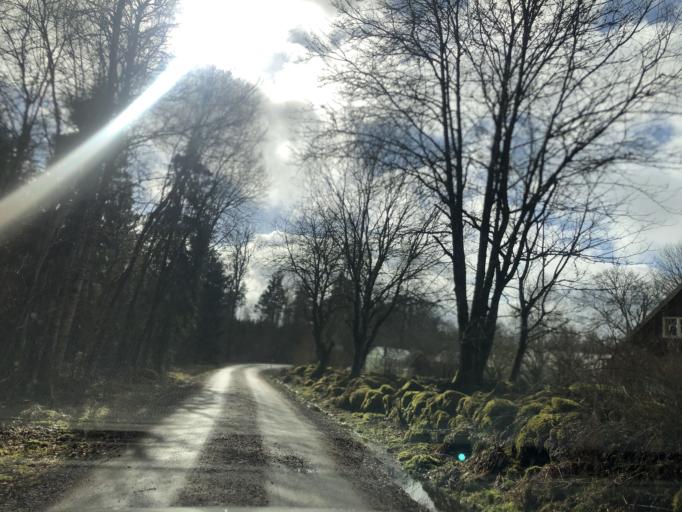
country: SE
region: Vaestra Goetaland
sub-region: Boras Kommun
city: Dalsjofors
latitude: 57.8262
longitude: 13.2208
